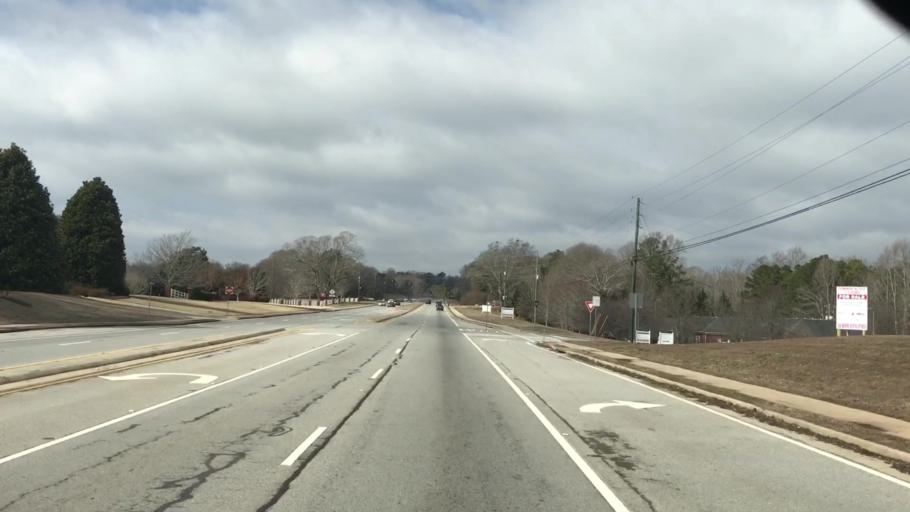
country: US
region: Georgia
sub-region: Hall County
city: Oakwood
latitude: 34.1793
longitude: -83.8441
